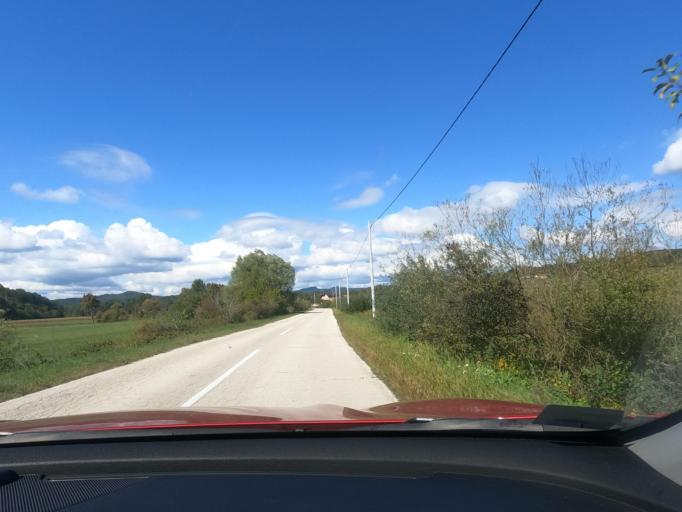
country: BA
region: Federation of Bosnia and Herzegovina
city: Podzvizd
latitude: 45.2272
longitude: 15.9069
